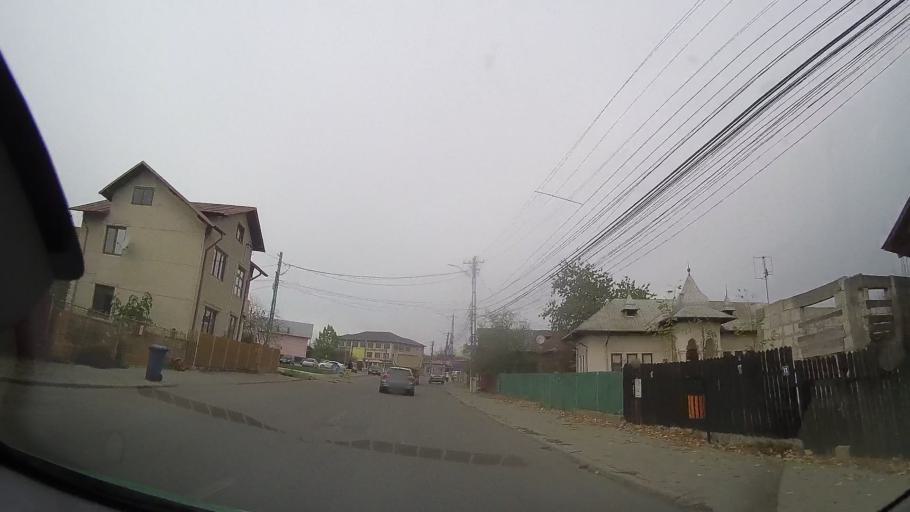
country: RO
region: Prahova
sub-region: Oras Baicoi
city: Liliesti
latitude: 45.0337
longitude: 25.8850
